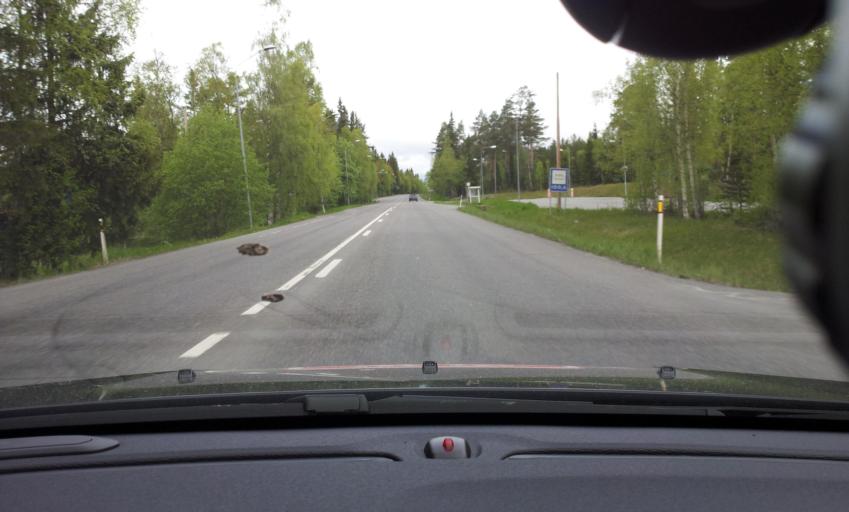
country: SE
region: Jaemtland
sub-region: OEstersunds Kommun
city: Brunflo
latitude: 63.0894
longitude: 14.8084
